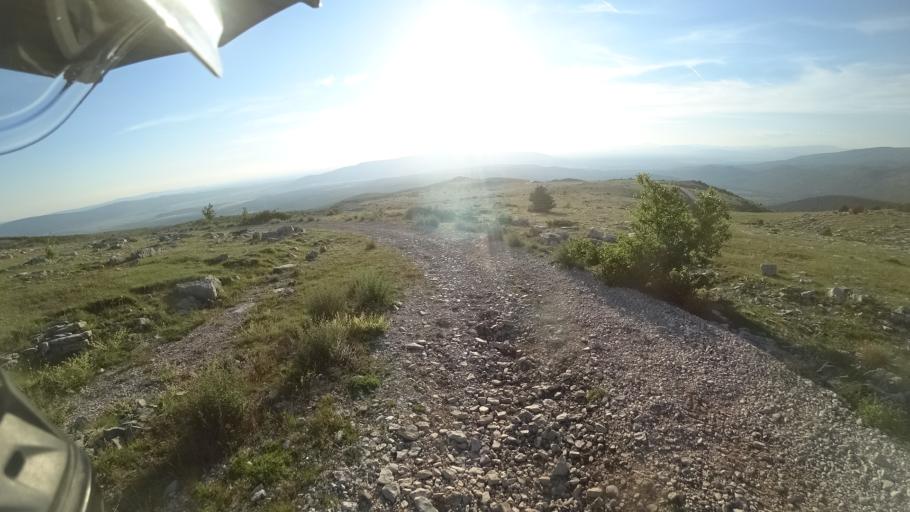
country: HR
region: Sibensko-Kniniska
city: Drnis
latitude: 43.8858
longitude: 16.3377
